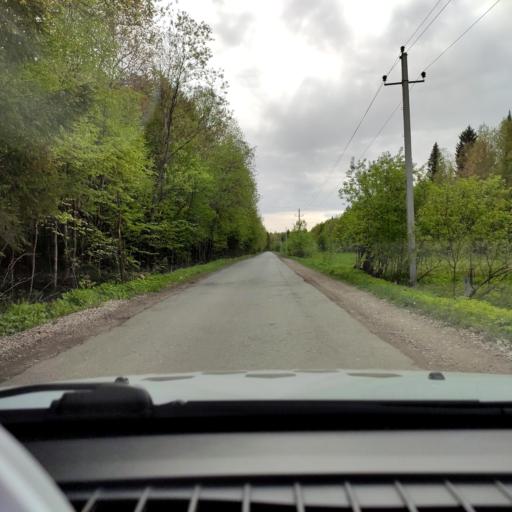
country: RU
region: Perm
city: Novyye Lyady
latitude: 58.0427
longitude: 56.6321
